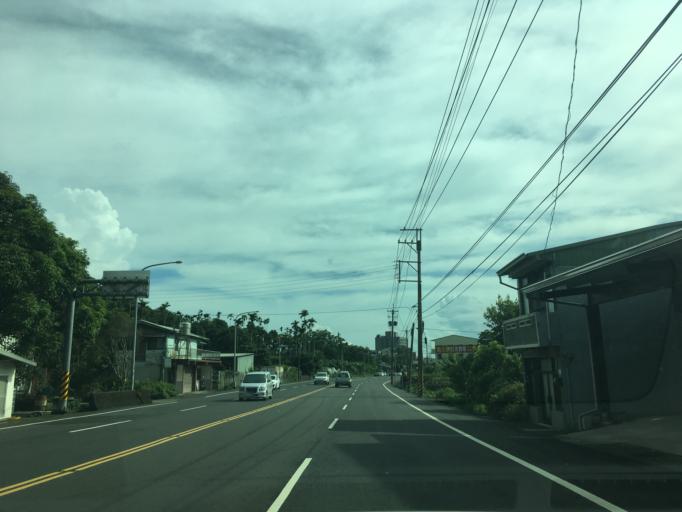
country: TW
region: Taiwan
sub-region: Chiayi
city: Jiayi Shi
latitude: 23.4486
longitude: 120.5483
